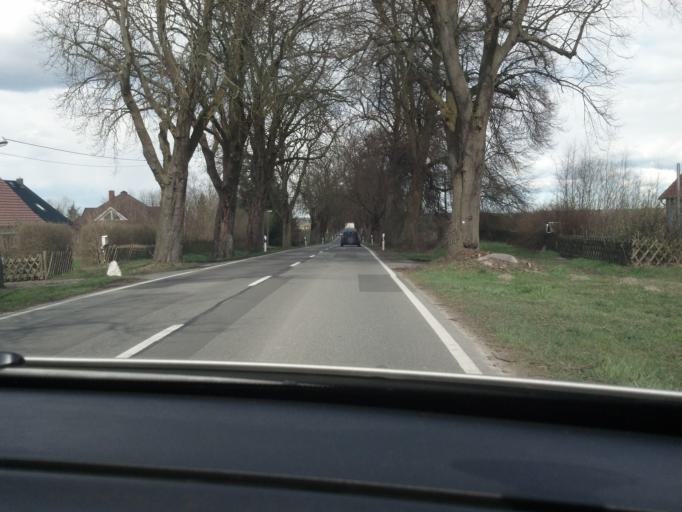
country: DE
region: Mecklenburg-Vorpommern
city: Loitz
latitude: 53.4442
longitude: 13.3484
